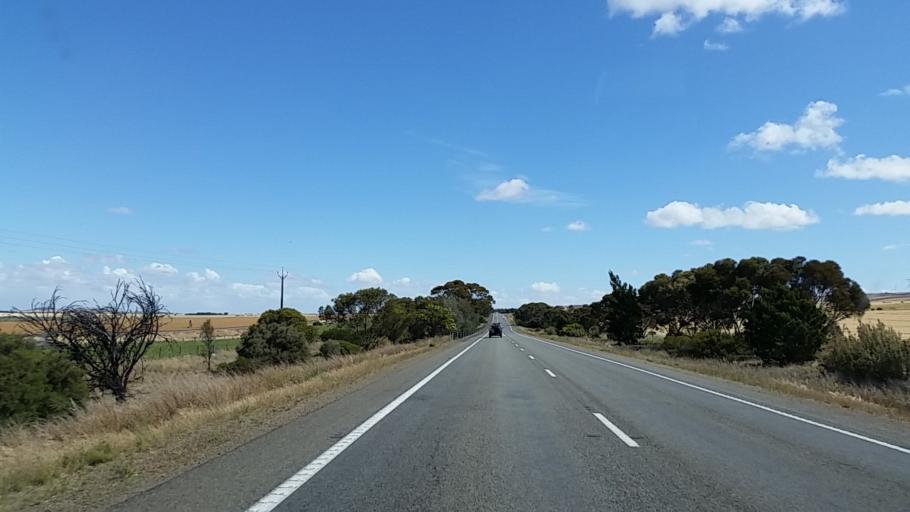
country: AU
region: South Australia
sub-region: Port Pirie City and Dists
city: Crystal Brook
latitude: -33.6625
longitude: 138.2247
